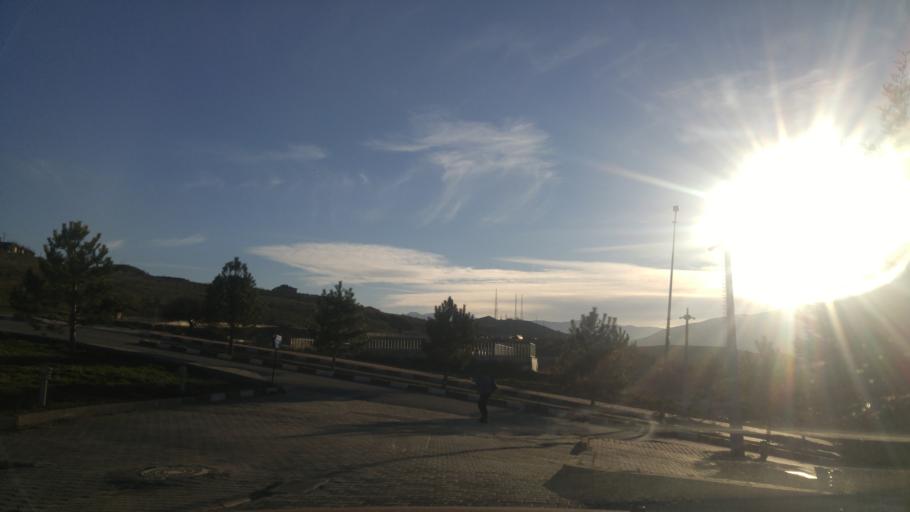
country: TR
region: Karabuk
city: Karabuk
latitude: 41.2051
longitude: 32.6593
